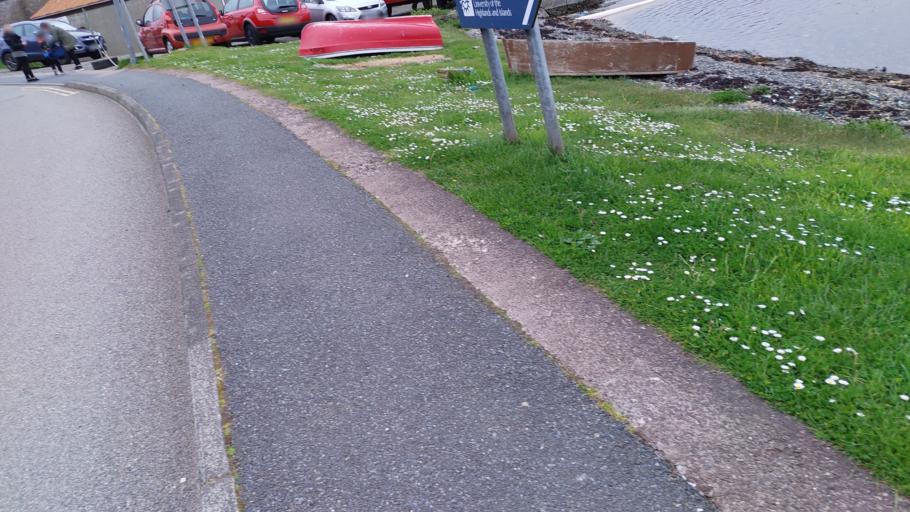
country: GB
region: Scotland
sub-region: Shetland Islands
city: Lerwick
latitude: 60.1367
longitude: -1.2827
